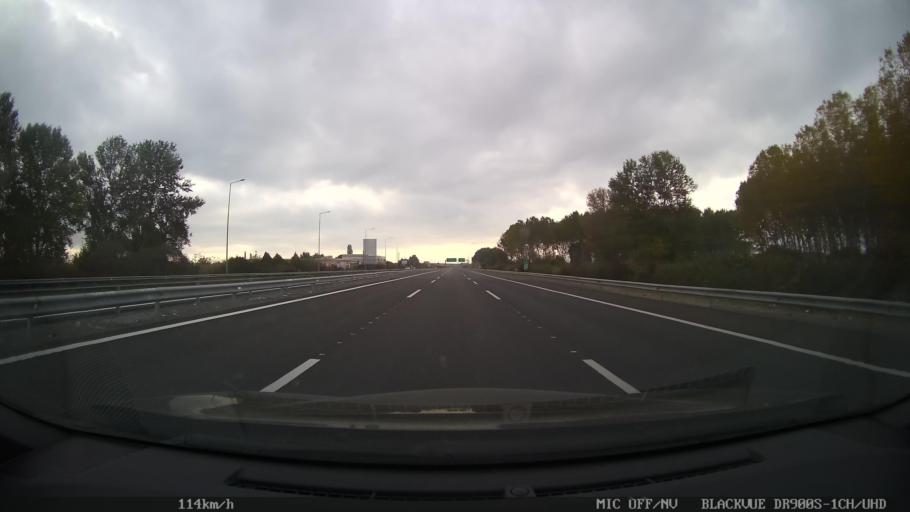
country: GR
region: Central Macedonia
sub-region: Nomos Pierias
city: Nea Efesos
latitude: 40.2013
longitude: 22.5469
